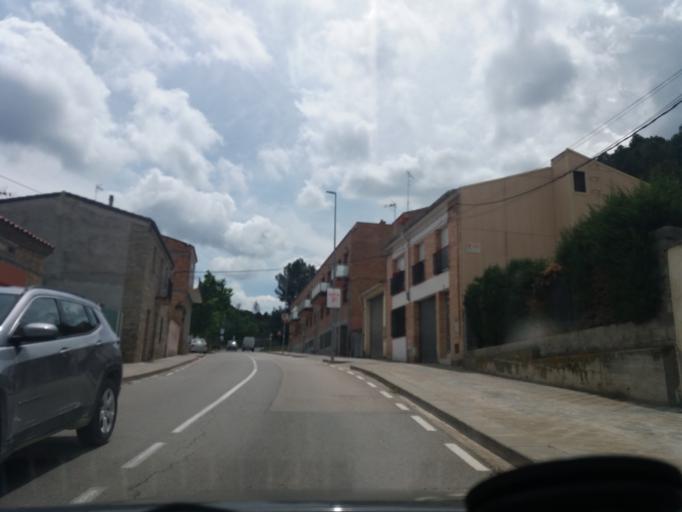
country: ES
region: Catalonia
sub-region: Provincia de Barcelona
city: Manresa
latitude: 41.6779
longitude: 1.8458
